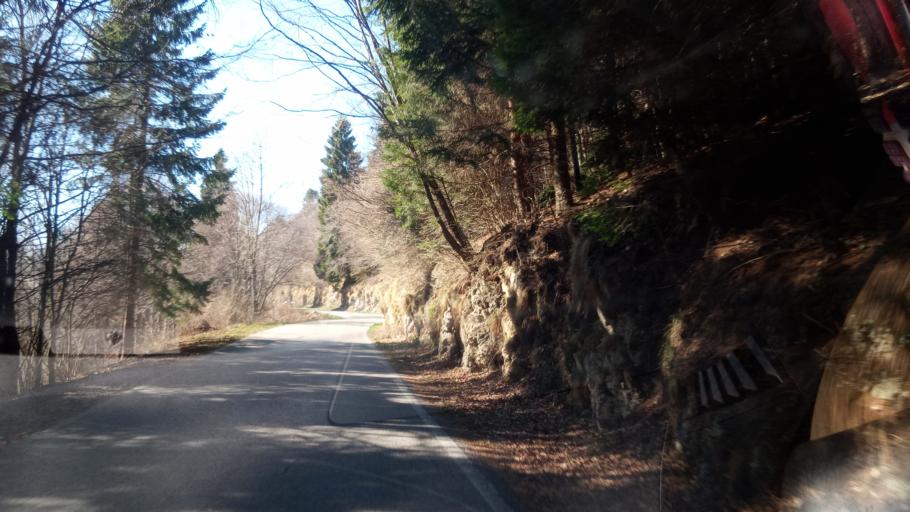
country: IT
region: Veneto
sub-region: Provincia di Treviso
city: Borso del Grappa
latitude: 45.8382
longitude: 11.7779
